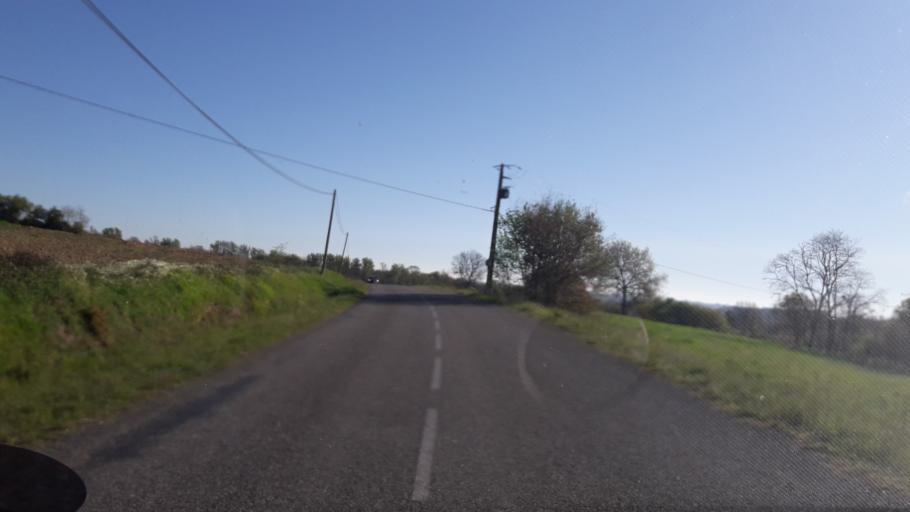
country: FR
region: Midi-Pyrenees
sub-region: Departement de la Haute-Garonne
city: Cazeres
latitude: 43.1987
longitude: 1.1533
